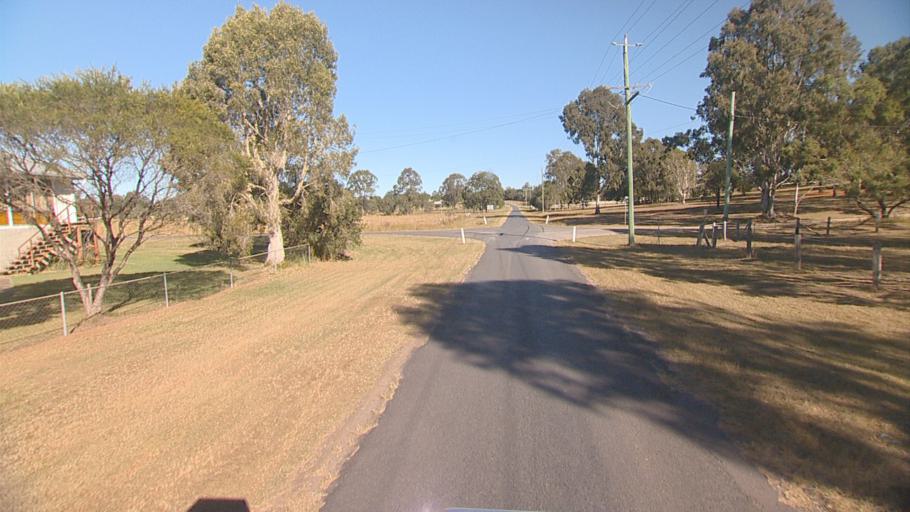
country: AU
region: Queensland
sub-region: Logan
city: North Maclean
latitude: -27.7794
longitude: 153.0193
